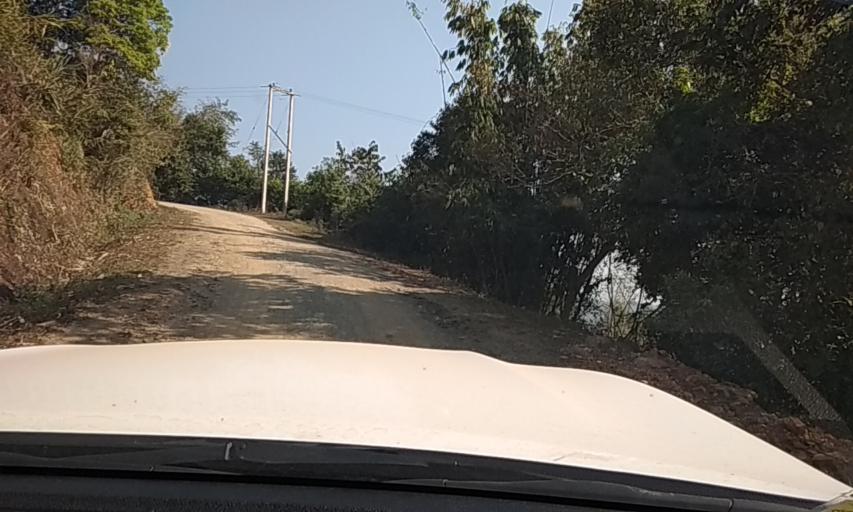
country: LA
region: Phongsali
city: Phongsali
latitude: 21.6962
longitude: 102.0833
